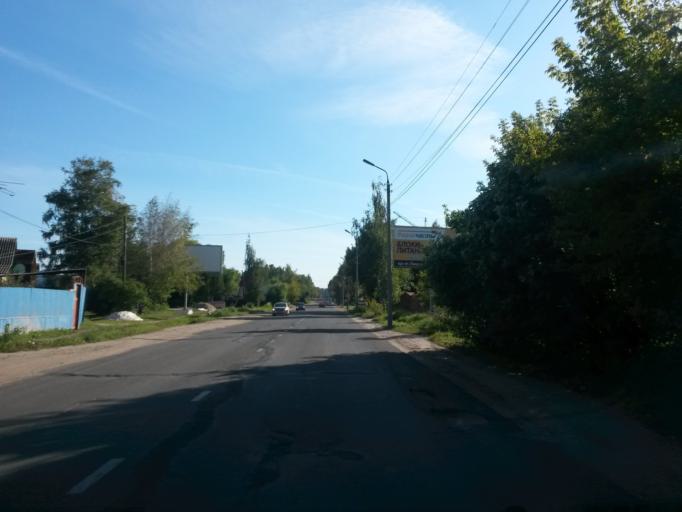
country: RU
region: Jaroslavl
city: Yaroslavl
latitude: 57.5825
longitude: 39.8724
